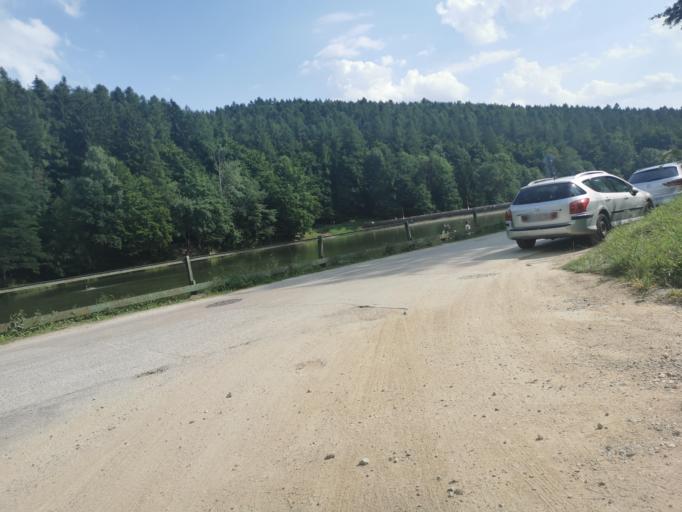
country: SK
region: Trenciansky
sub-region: Okres Myjava
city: Myjava
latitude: 48.8106
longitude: 17.5954
